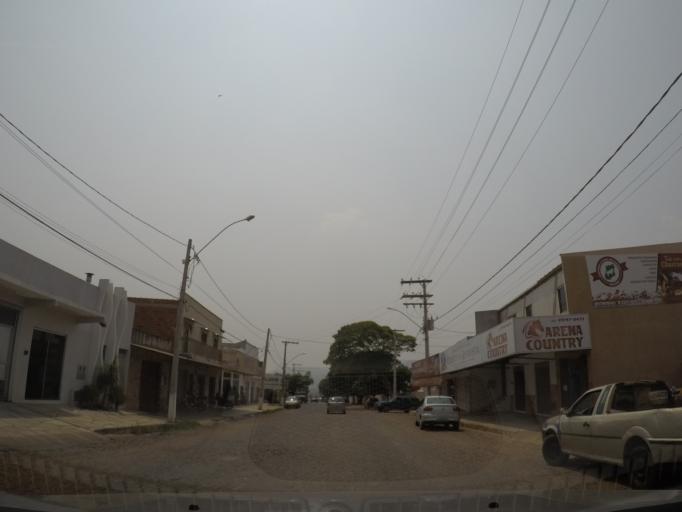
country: BR
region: Goias
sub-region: Pirenopolis
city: Pirenopolis
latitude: -15.8590
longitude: -48.9569
